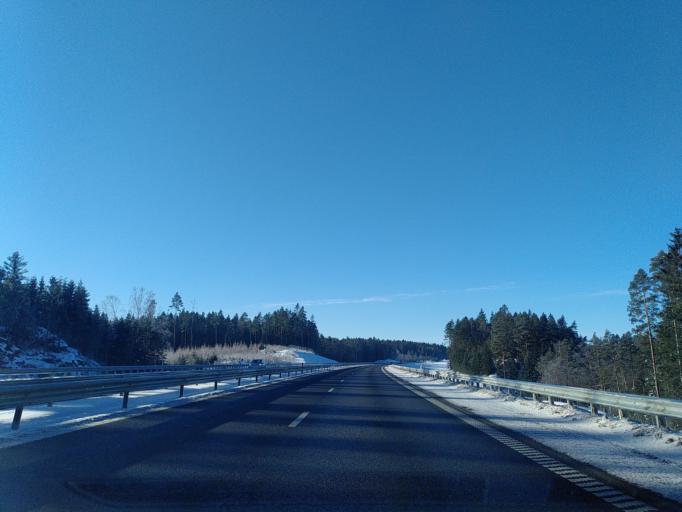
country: SE
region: Vaestra Goetaland
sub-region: Vargarda Kommun
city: Jonstorp
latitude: 57.9753
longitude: 12.7054
